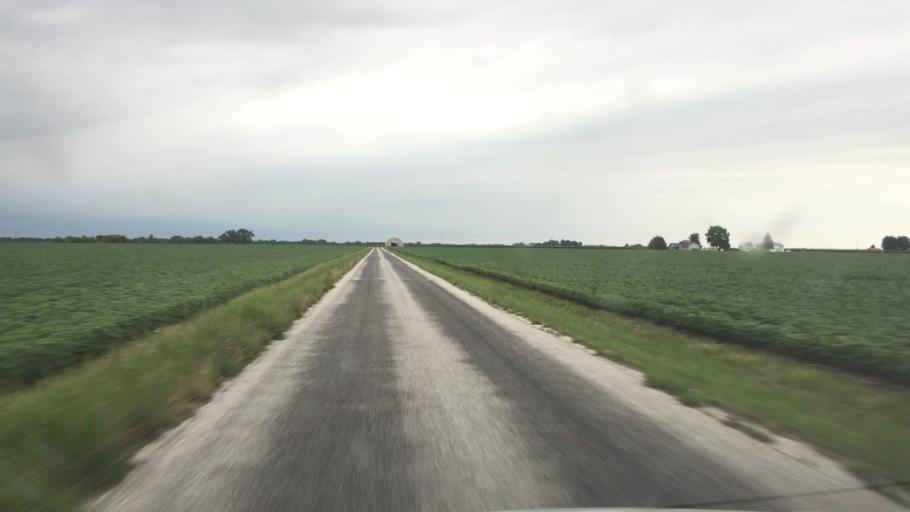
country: US
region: Illinois
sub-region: Adams County
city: Camp Point
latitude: 40.2240
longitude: -90.9691
